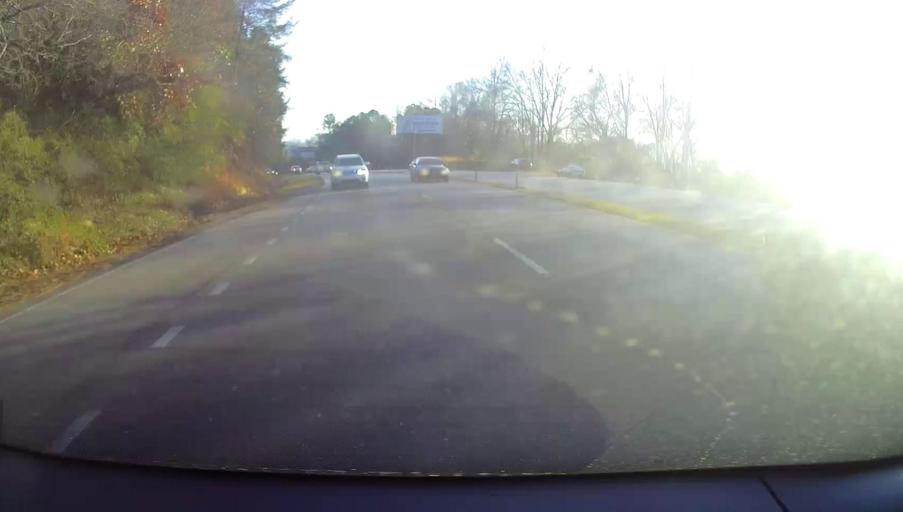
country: US
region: Alabama
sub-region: Calhoun County
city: Anniston
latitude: 33.6766
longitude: -85.8276
